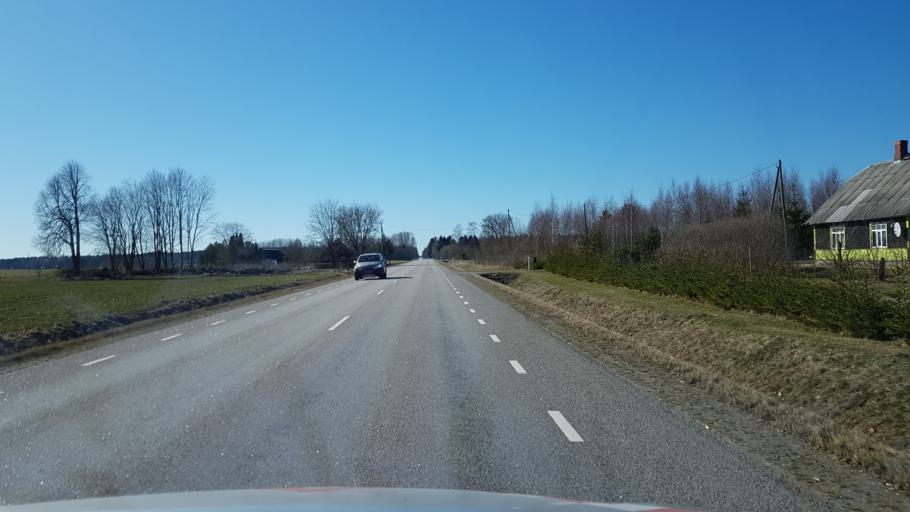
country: EE
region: Laeaene-Virumaa
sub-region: Viru-Nigula vald
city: Kunda
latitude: 59.3541
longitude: 26.6698
